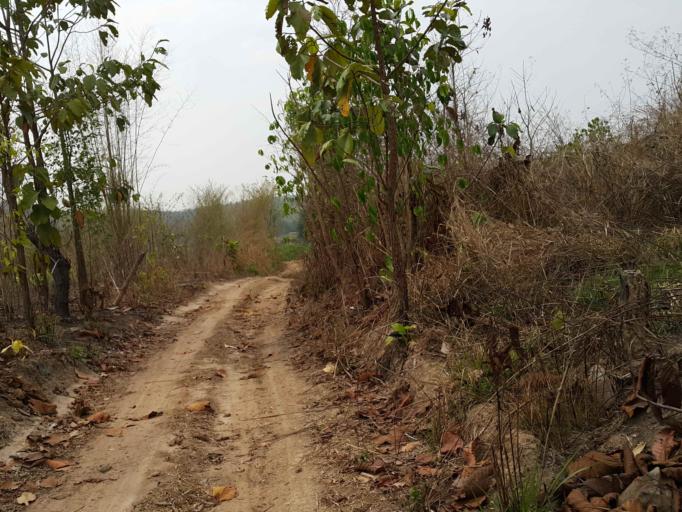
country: TH
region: Chiang Mai
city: Mae Taeng
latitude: 19.1095
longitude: 98.9860
